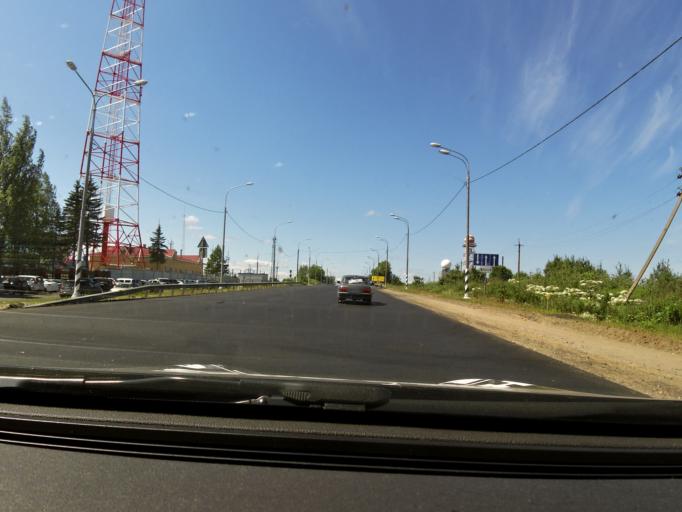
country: RU
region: Novgorod
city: Valday
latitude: 57.9525
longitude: 33.2824
